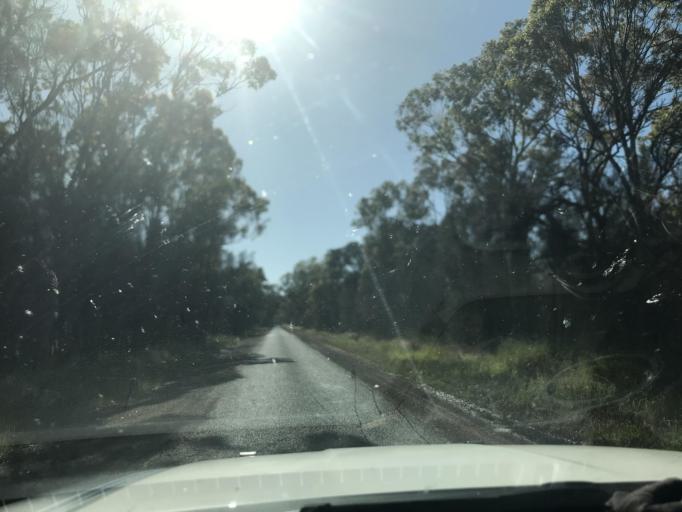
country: AU
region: Victoria
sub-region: Horsham
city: Horsham
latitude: -37.0071
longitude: 141.6419
